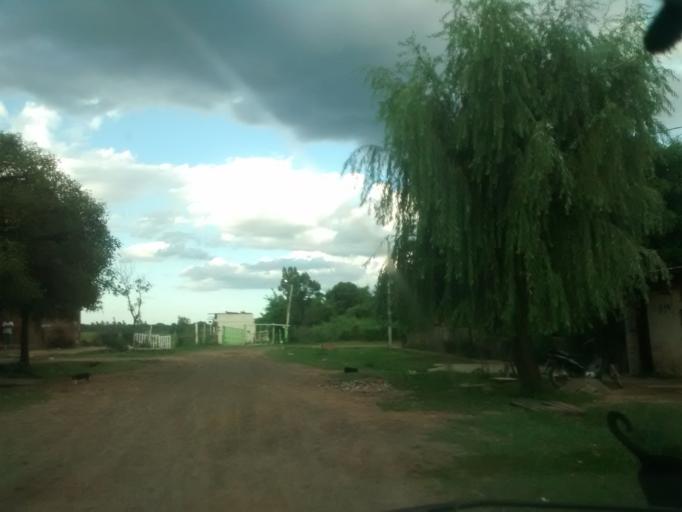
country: AR
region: Chaco
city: Fontana
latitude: -27.4271
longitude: -58.9948
